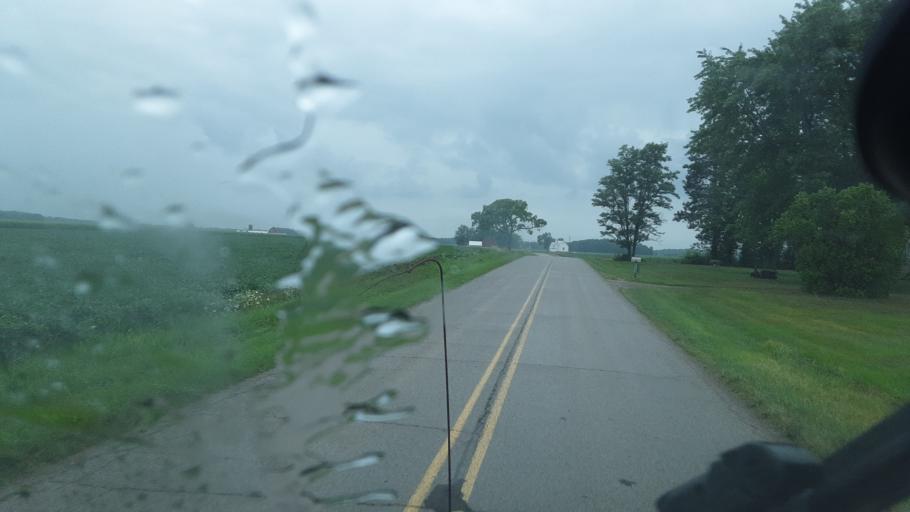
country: US
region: Ohio
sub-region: Williams County
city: Edgerton
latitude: 41.5013
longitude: -84.8070
